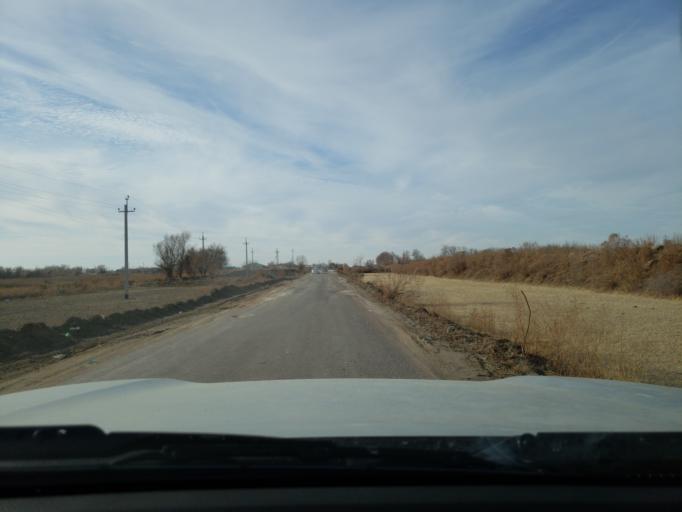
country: TM
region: Dasoguz
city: Dasoguz
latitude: 41.8492
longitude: 59.8845
